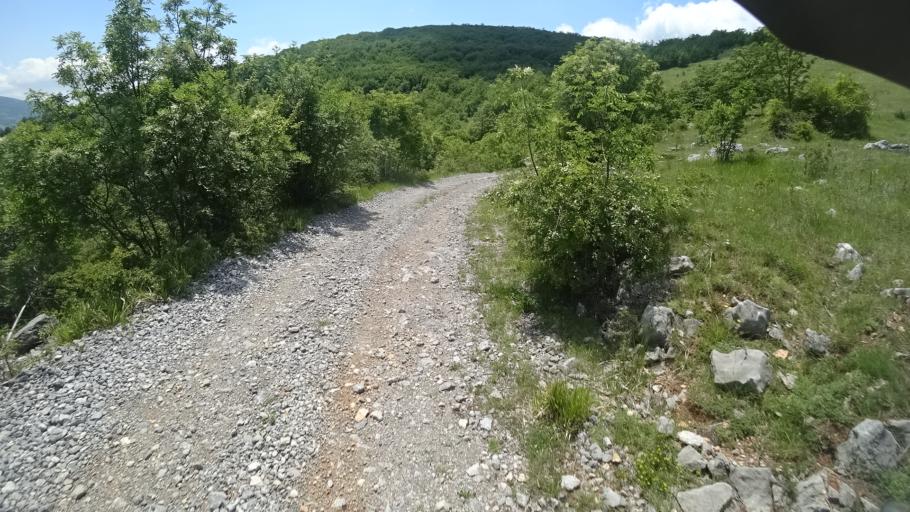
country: HR
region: Zadarska
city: Gracac
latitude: 44.4464
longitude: 15.9132
